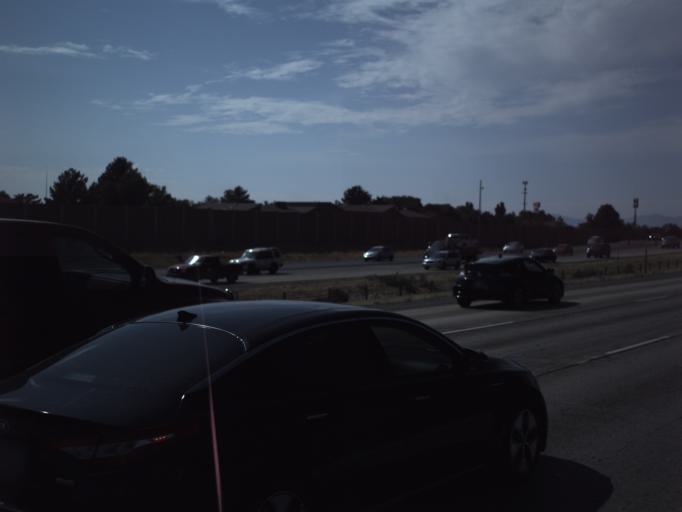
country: US
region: Utah
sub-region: Davis County
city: Clearfield
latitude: 41.1202
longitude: -112.0190
